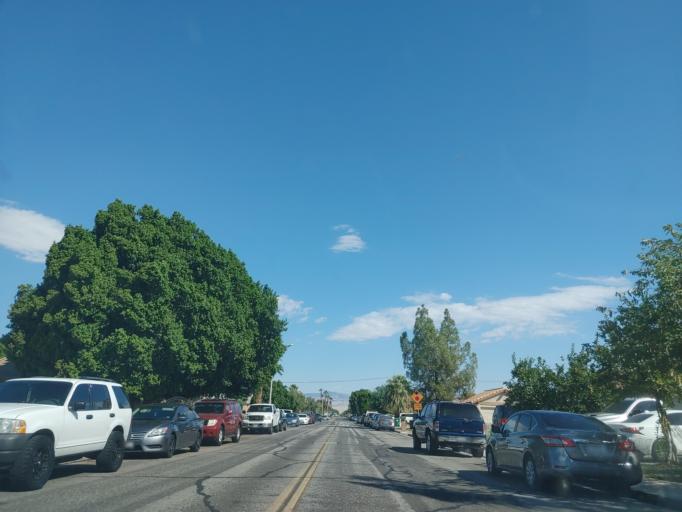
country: US
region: California
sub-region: Riverside County
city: Cathedral City
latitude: 33.8039
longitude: -116.4701
